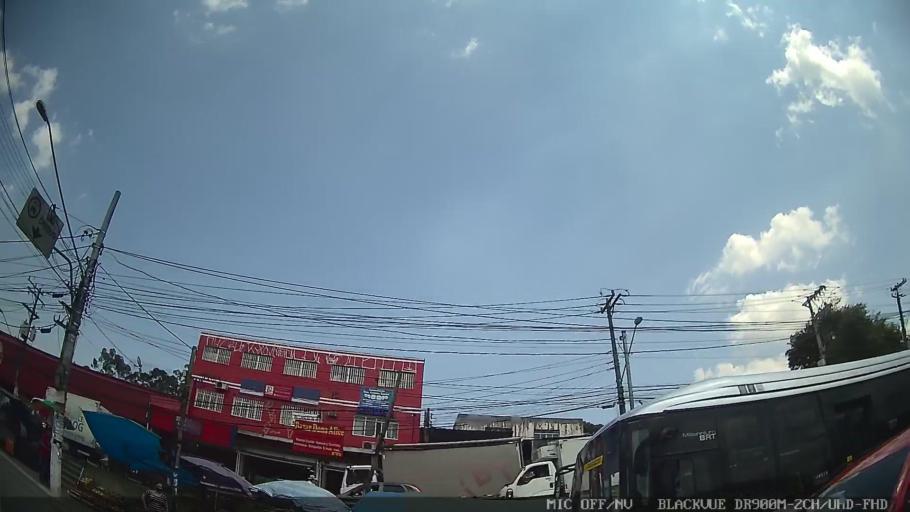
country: BR
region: Sao Paulo
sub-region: Itapecerica Da Serra
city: Itapecerica da Serra
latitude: -23.6856
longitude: -46.8009
